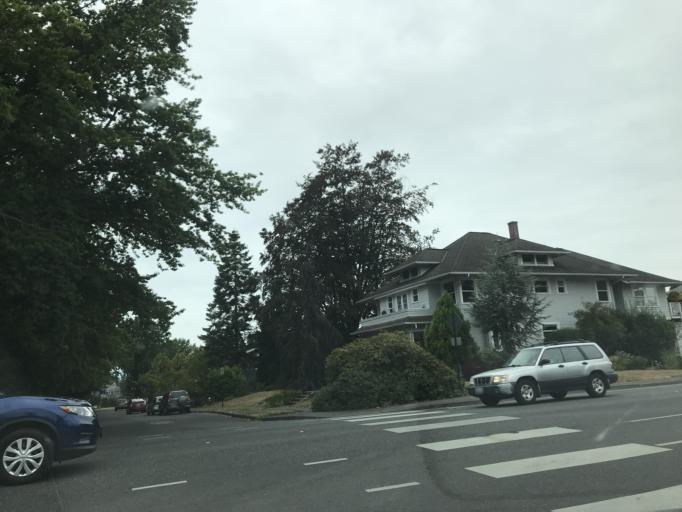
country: US
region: Washington
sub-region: Whatcom County
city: Bellingham
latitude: 48.7668
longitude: -122.4765
